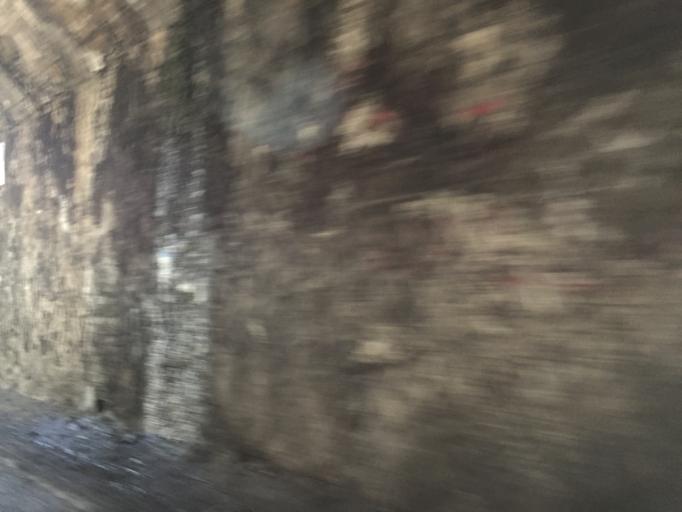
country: GB
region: England
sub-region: Bristol
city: Bristol
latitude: 51.4511
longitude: -2.5780
